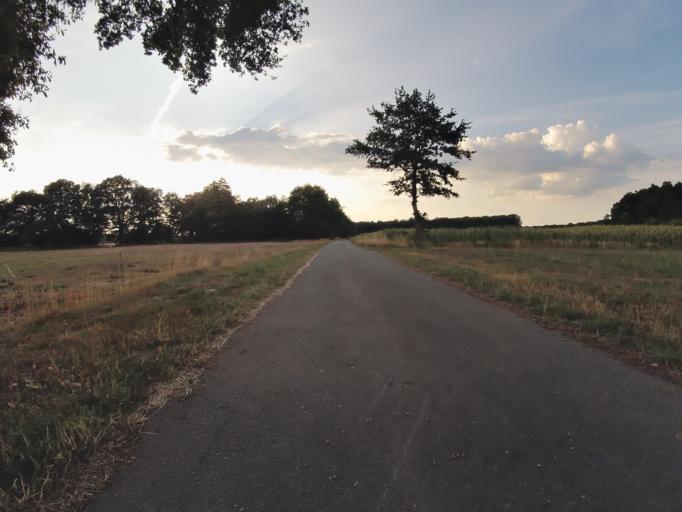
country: DE
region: North Rhine-Westphalia
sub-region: Regierungsbezirk Munster
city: Westerkappeln
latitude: 52.3647
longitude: 7.8757
